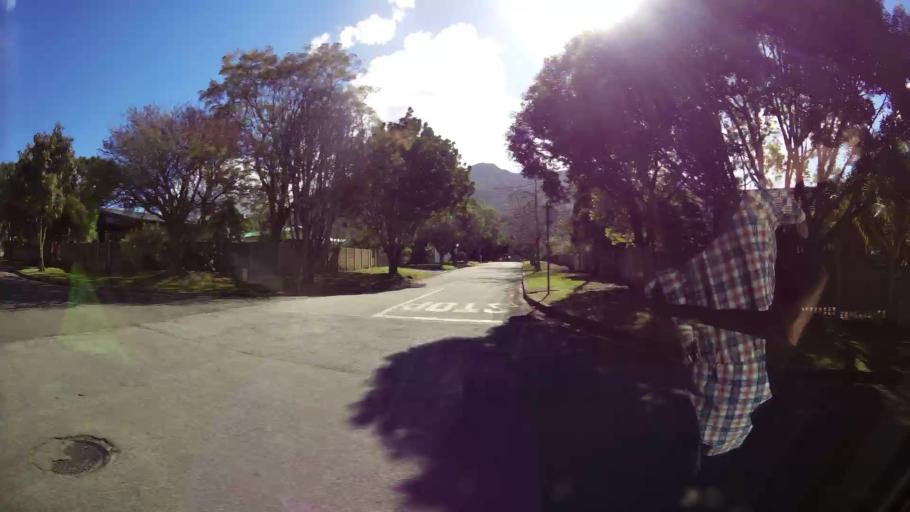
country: ZA
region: Western Cape
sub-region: Eden District Municipality
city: George
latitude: -33.9437
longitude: 22.4774
